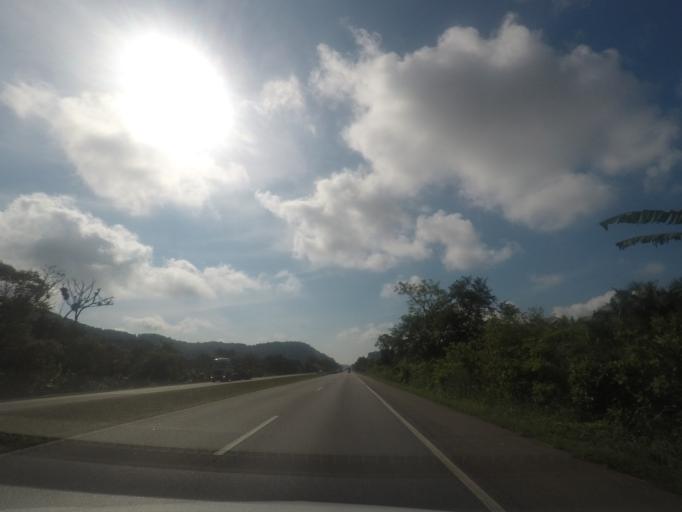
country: BR
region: Parana
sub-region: Antonina
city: Antonina
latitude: -25.5380
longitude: -48.7700
